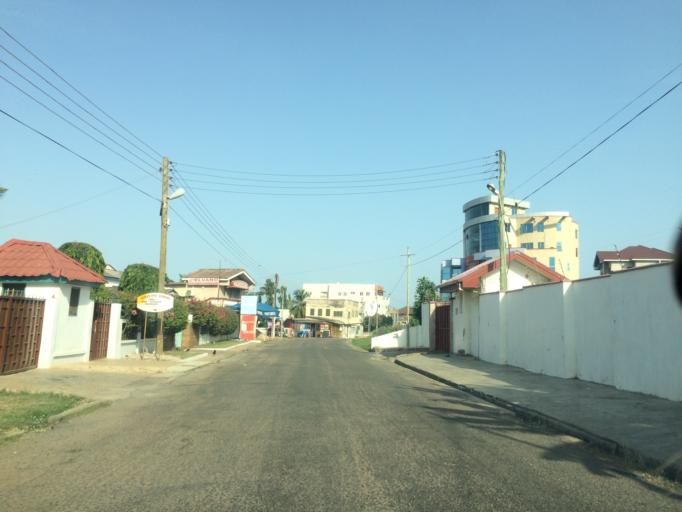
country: GH
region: Greater Accra
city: Accra
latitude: 5.5637
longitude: -0.1853
